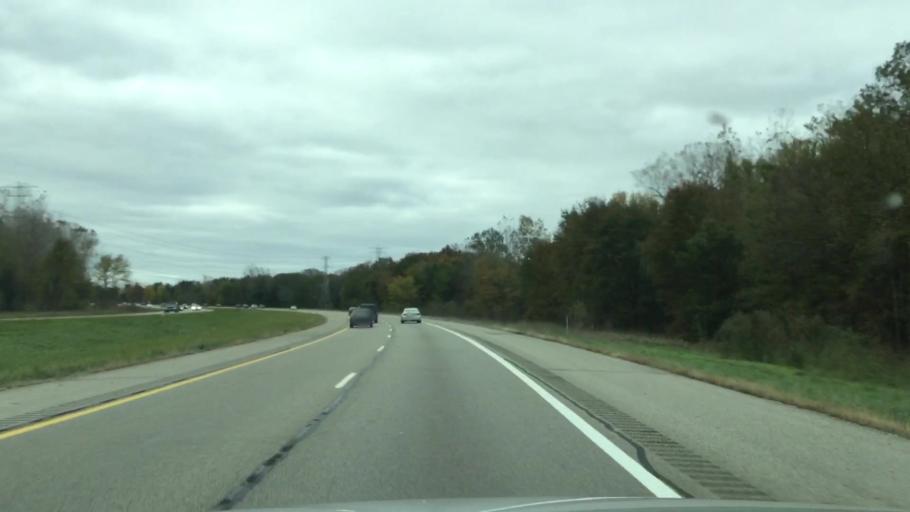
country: US
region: Michigan
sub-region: Wayne County
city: Canton
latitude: 42.3575
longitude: -83.5836
